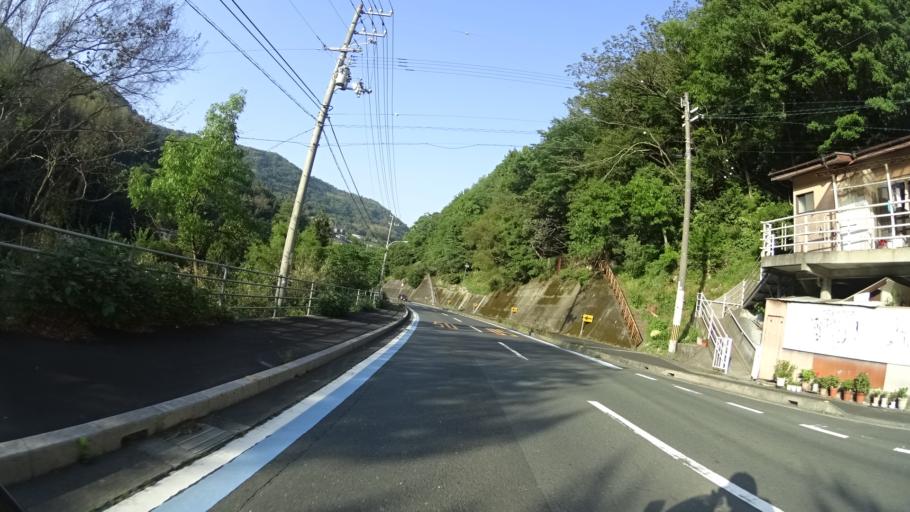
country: JP
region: Ehime
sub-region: Nishiuwa-gun
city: Ikata-cho
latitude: 33.4969
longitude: 132.3685
